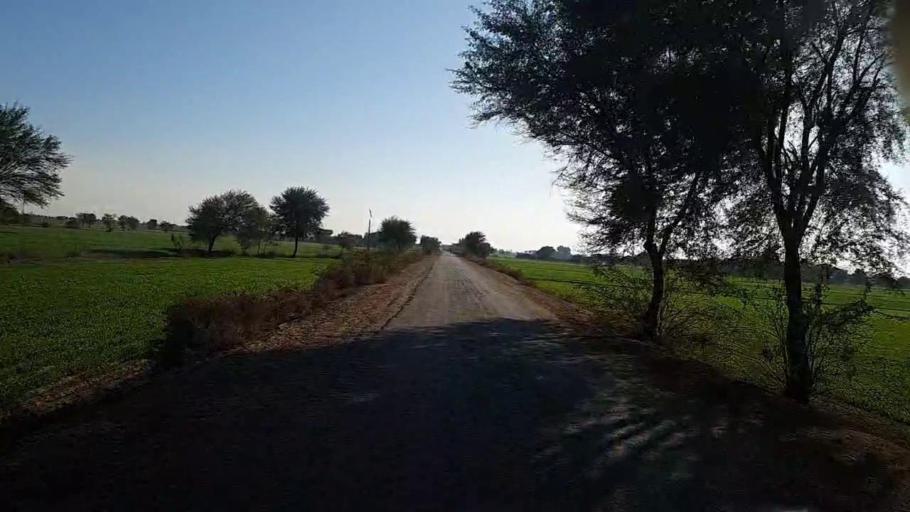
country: PK
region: Sindh
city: Khairpur
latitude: 27.8982
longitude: 69.7477
